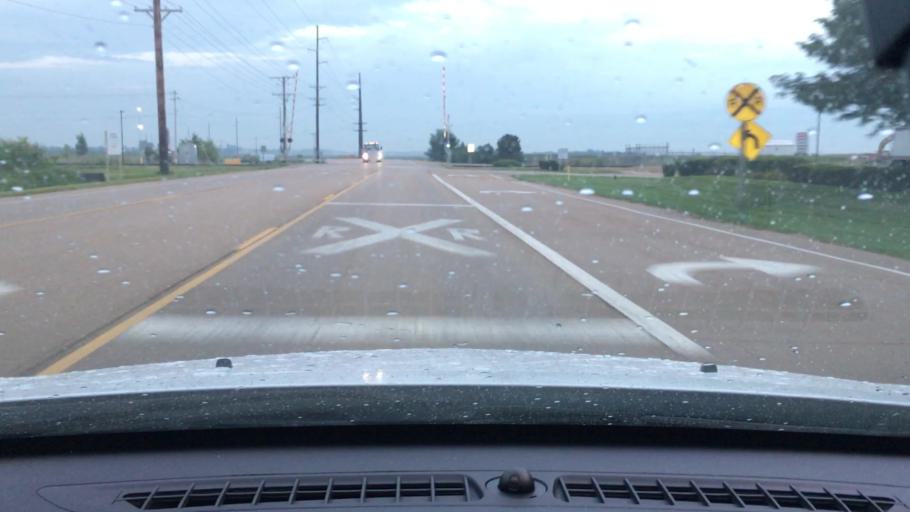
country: US
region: Illinois
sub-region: Ogle County
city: Rochelle
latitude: 41.8931
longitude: -89.0294
